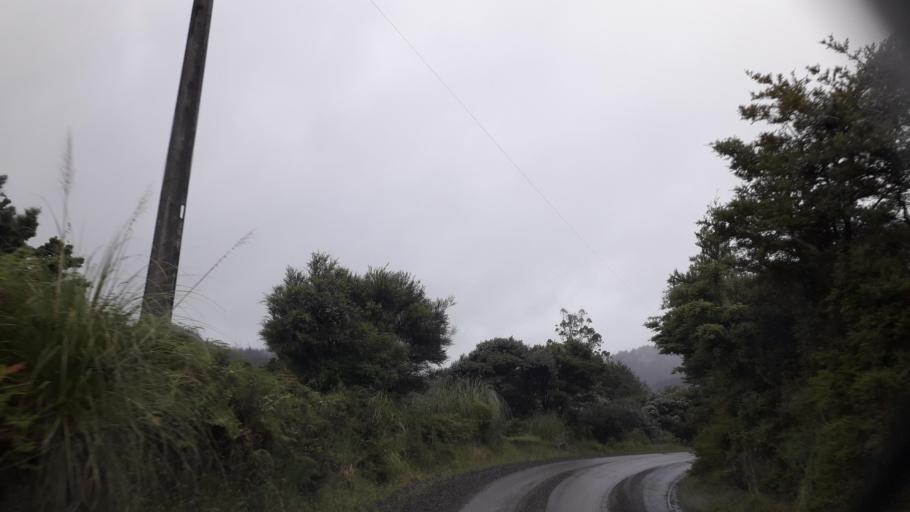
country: NZ
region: Northland
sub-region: Far North District
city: Kaitaia
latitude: -35.3807
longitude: 173.4097
